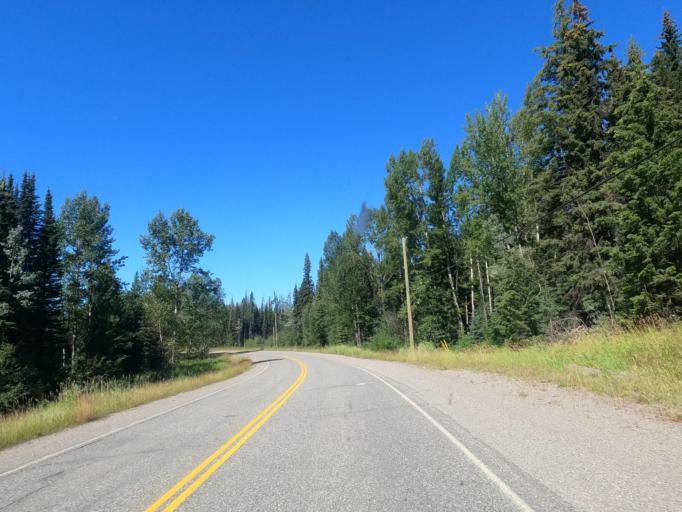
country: CA
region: British Columbia
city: Quesnel
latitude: 53.0429
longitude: -122.2520
